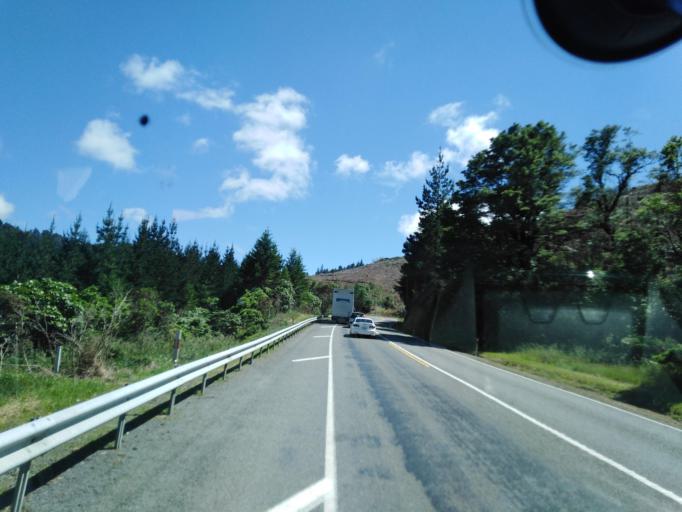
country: NZ
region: Nelson
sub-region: Nelson City
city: Nelson
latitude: -41.1957
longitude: 173.5581
